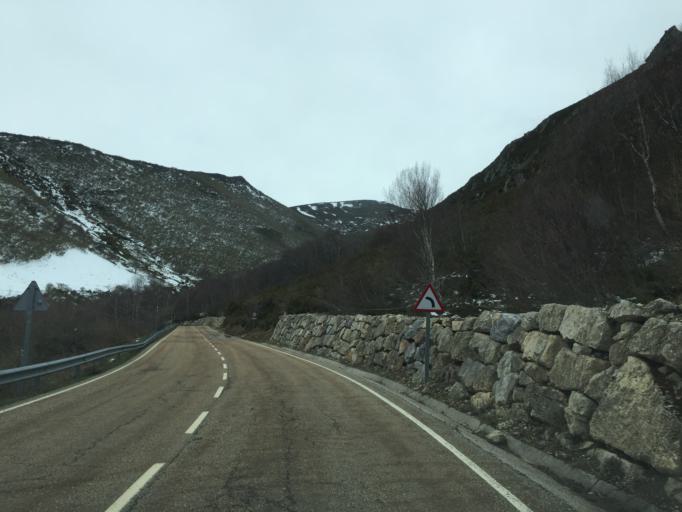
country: ES
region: Castille and Leon
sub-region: Provincia de Leon
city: San Emiliano
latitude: 43.0495
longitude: -6.0208
